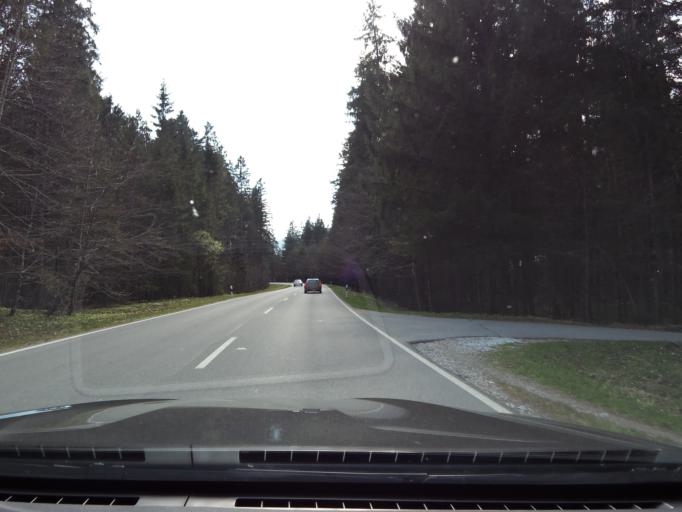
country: DE
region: Bavaria
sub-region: Upper Bavaria
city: Wallgau
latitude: 47.5598
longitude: 11.2939
